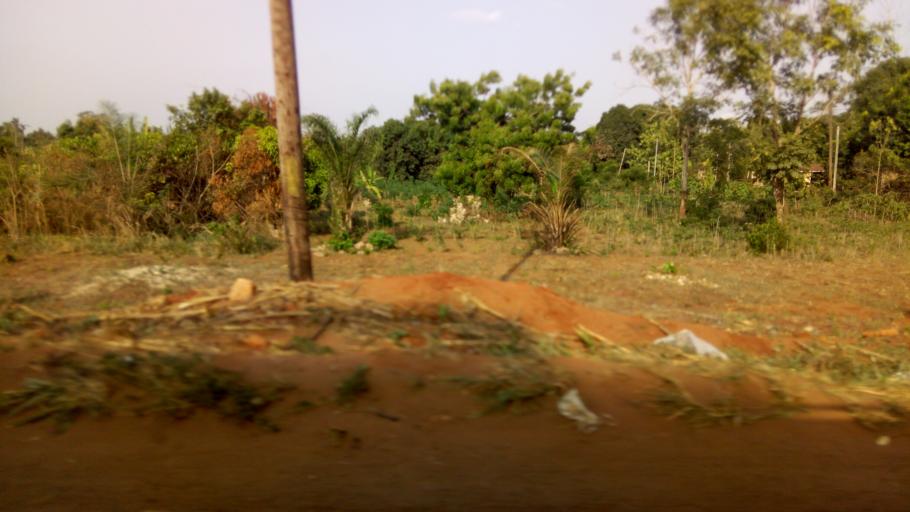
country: TG
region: Maritime
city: Tsevie
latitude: 6.3817
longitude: 1.2036
